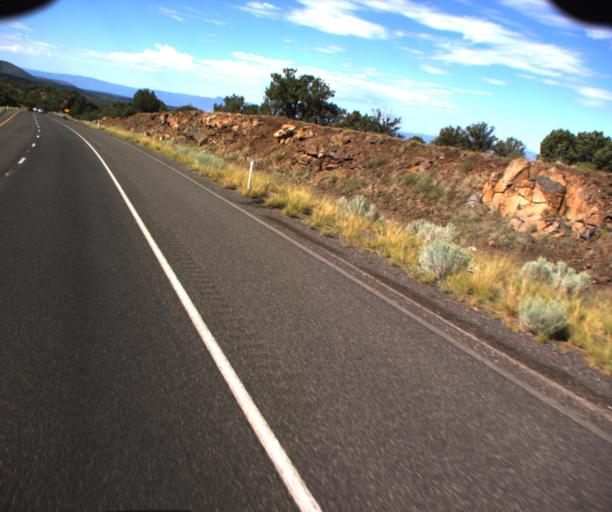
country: US
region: Arizona
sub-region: Yavapai County
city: Village of Oak Creek (Big Park)
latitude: 34.7964
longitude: -111.5998
